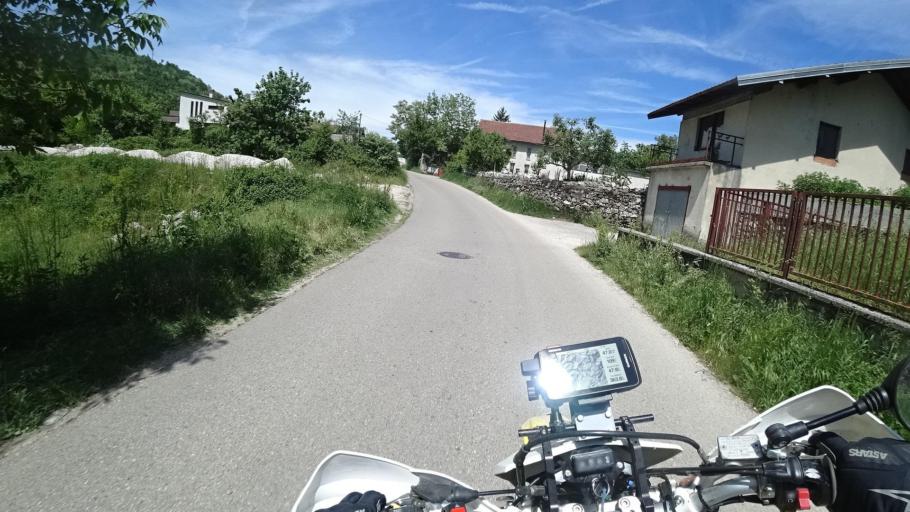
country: BA
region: Federation of Bosnia and Herzegovina
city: Polje-Bijela
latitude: 43.6242
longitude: 17.9676
